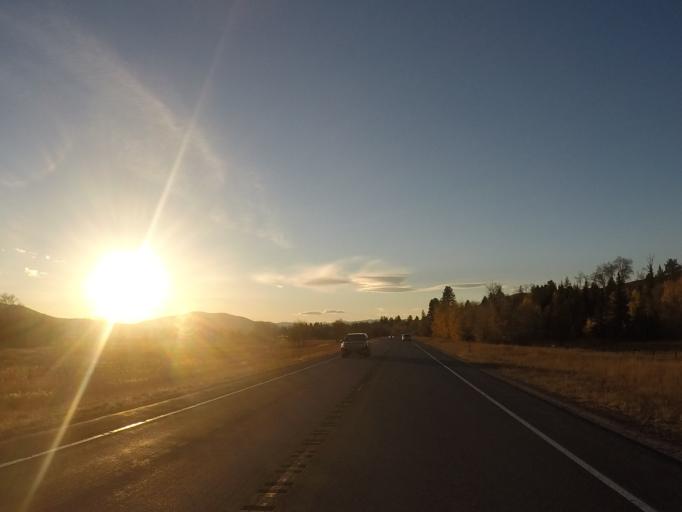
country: US
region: Montana
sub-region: Lewis and Clark County
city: Lincoln
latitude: 47.0168
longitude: -113.0779
